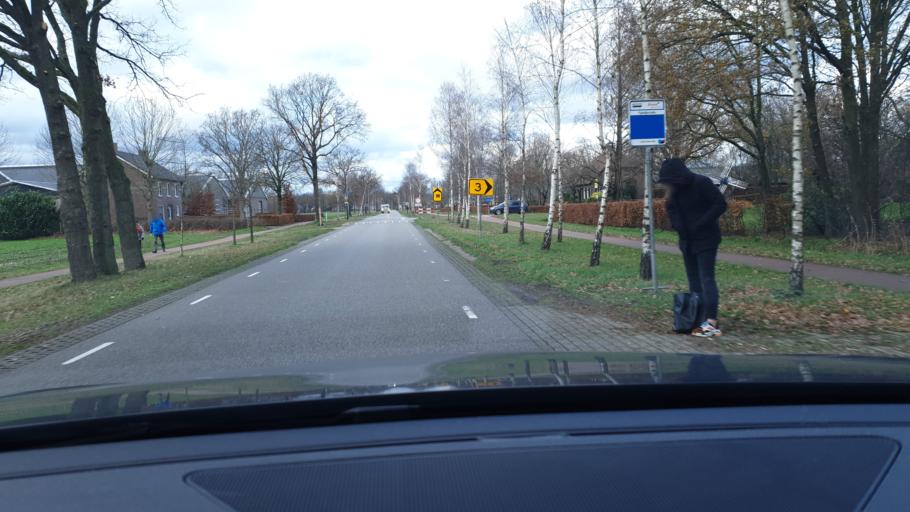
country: NL
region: North Brabant
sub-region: Gemeente Veldhoven
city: Veldhoven
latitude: 51.3880
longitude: 5.4092
